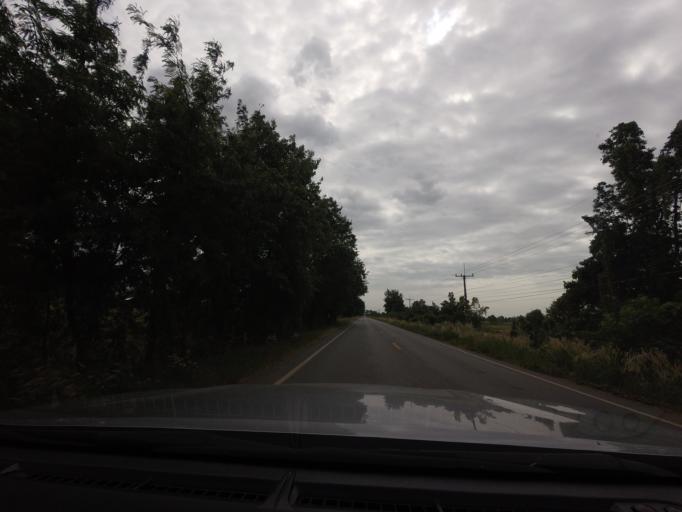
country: TH
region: Phitsanulok
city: Noen Maprang
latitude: 16.6611
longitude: 100.6153
